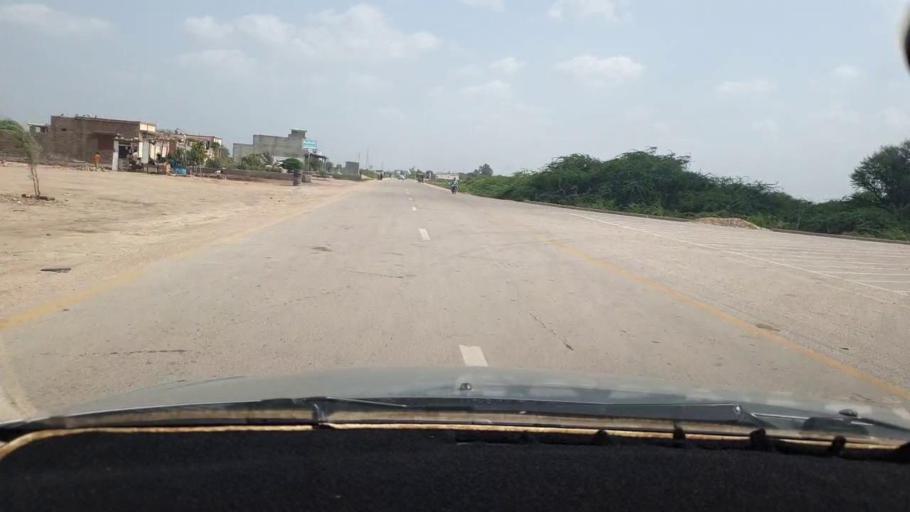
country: PK
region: Sindh
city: Digri
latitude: 25.0878
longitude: 69.1978
